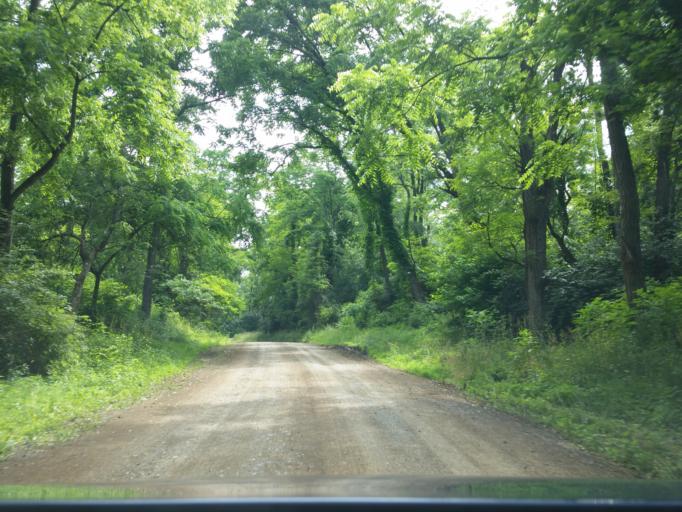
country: US
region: Pennsylvania
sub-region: Lebanon County
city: Jonestown
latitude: 40.4367
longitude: -76.5292
